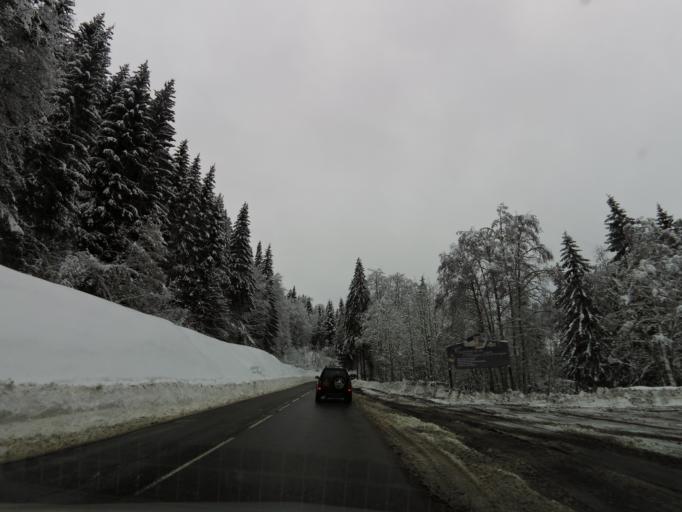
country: FR
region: Rhone-Alpes
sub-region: Departement de la Haute-Savoie
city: Les Gets
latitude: 46.1751
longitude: 6.6814
